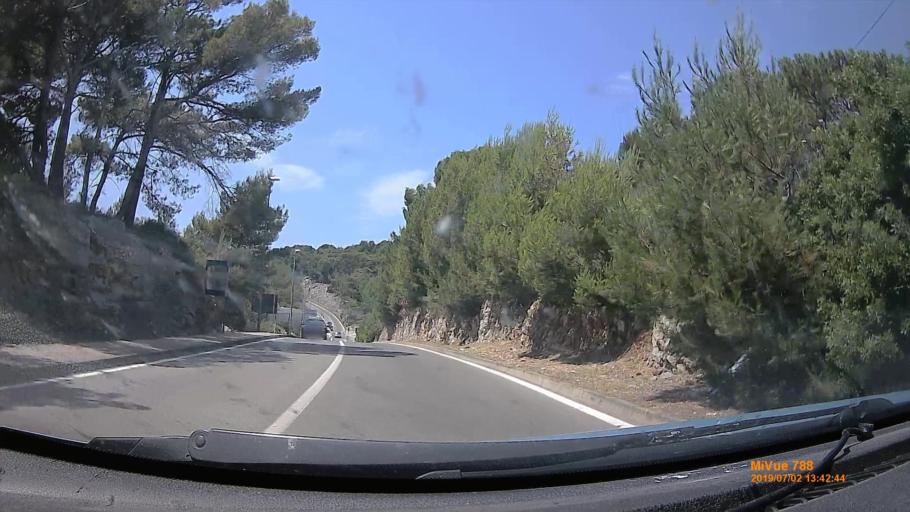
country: HR
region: Primorsko-Goranska
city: Mali Losinj
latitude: 44.5445
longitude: 14.4621
